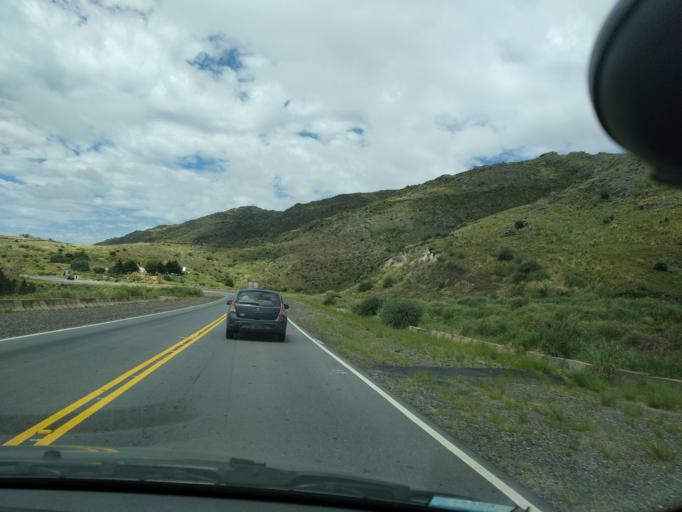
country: AR
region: Cordoba
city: Cuesta Blanca
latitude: -31.6177
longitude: -64.6871
